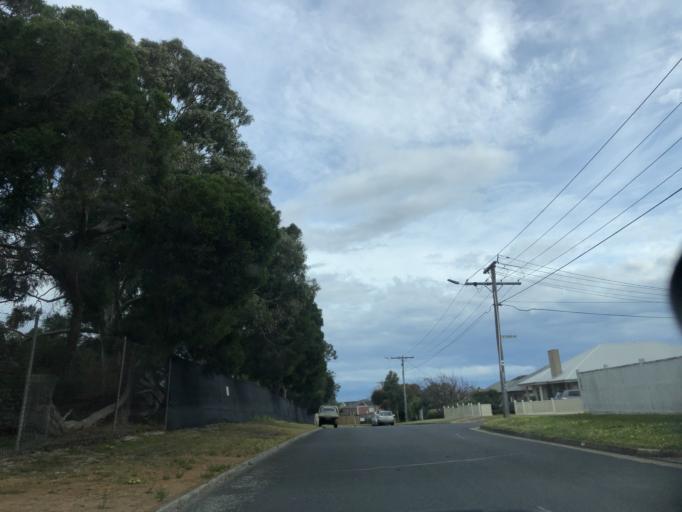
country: AU
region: Victoria
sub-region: Monash
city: Oakleigh South
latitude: -37.9282
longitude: 145.0851
